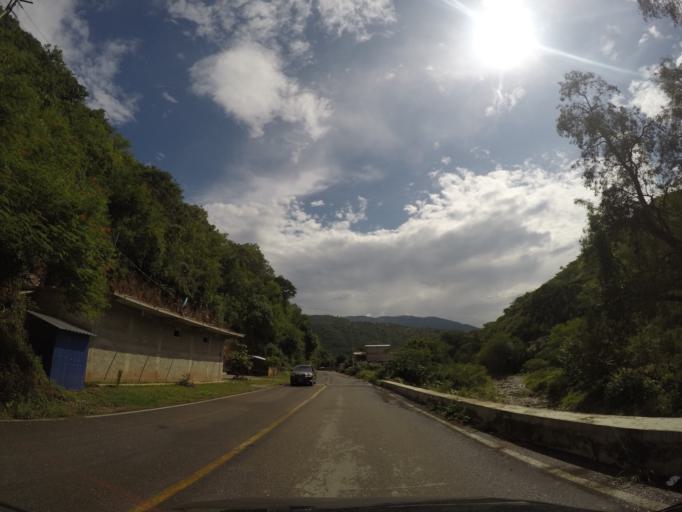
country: MX
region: Oaxaca
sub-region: San Jeronimo Coatlan
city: San Cristobal Honduras
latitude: 16.3577
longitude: -97.0932
